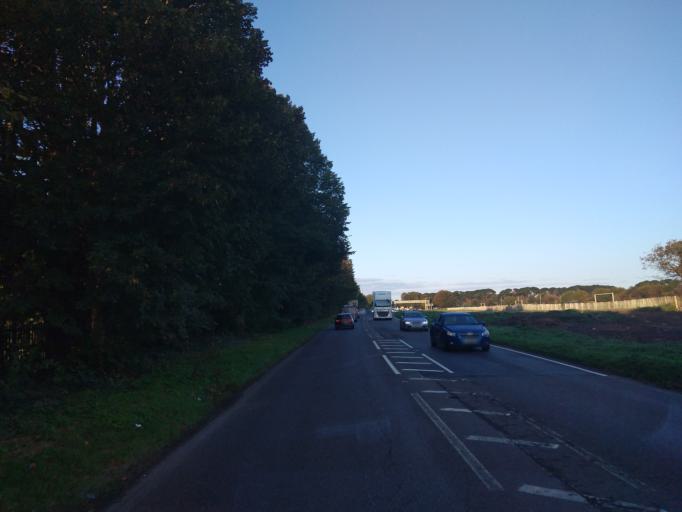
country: GB
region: England
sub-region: West Sussex
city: Rustington
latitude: 50.8182
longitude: -0.4834
